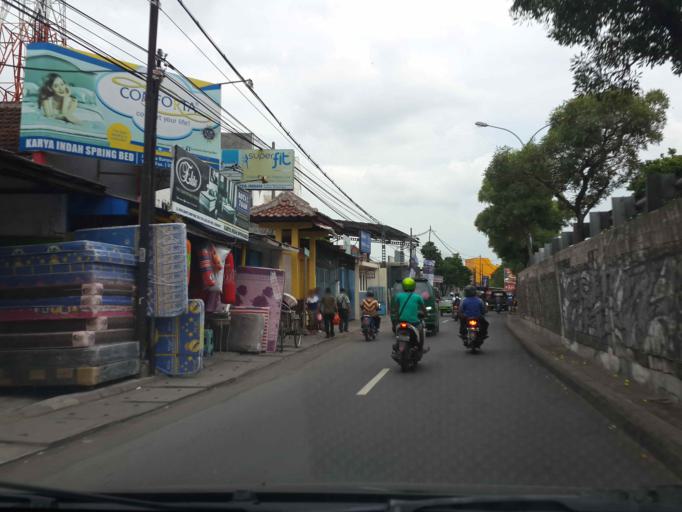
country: ID
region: East Java
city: Gubengairlangga
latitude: -7.2728
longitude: 112.7244
